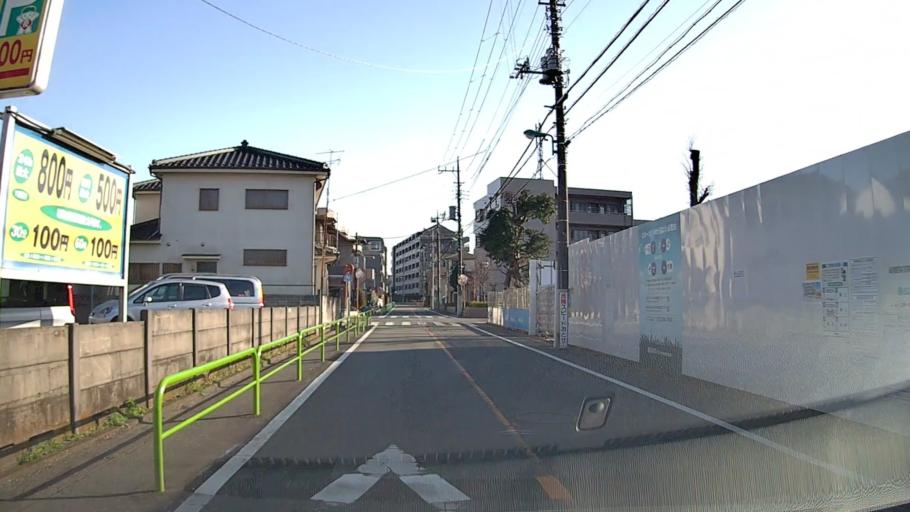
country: JP
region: Saitama
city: Wako
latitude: 35.7522
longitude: 139.6498
